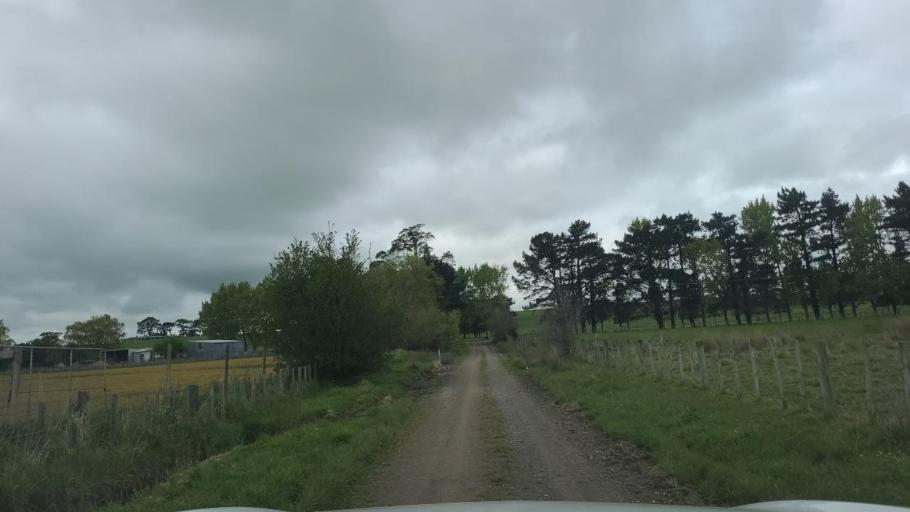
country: NZ
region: Wellington
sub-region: Masterton District
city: Masterton
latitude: -41.0514
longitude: 175.5197
